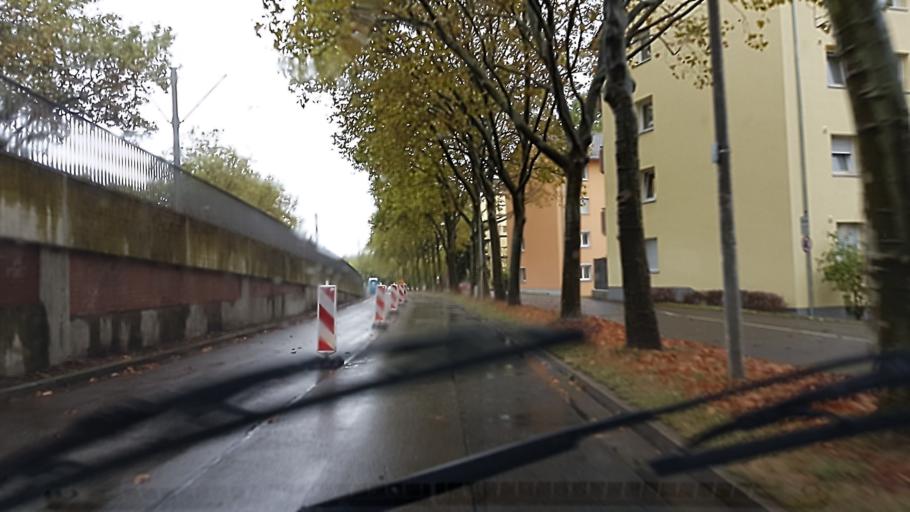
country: DE
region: Baden-Wuerttemberg
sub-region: Freiburg Region
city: Freiburg
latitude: 48.0053
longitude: 7.8219
